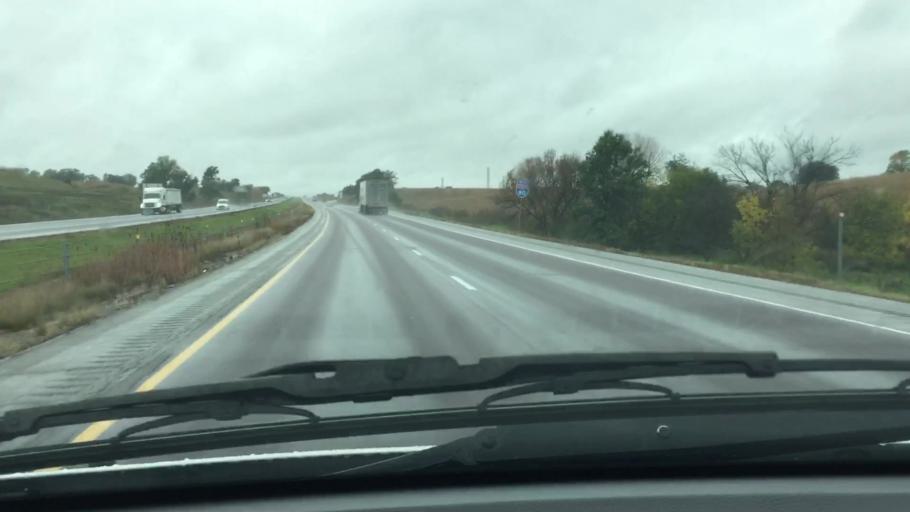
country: US
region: Iowa
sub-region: Poweshiek County
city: Montezuma
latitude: 41.6967
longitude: -92.5610
